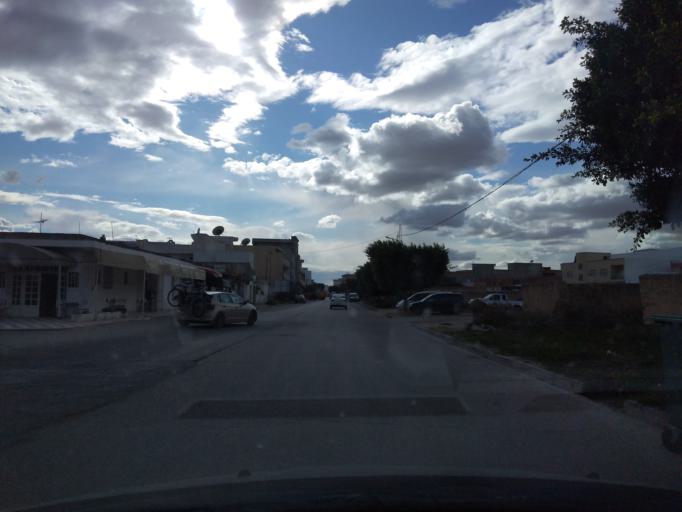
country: TN
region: Susah
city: Masakin
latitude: 35.7212
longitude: 10.5707
